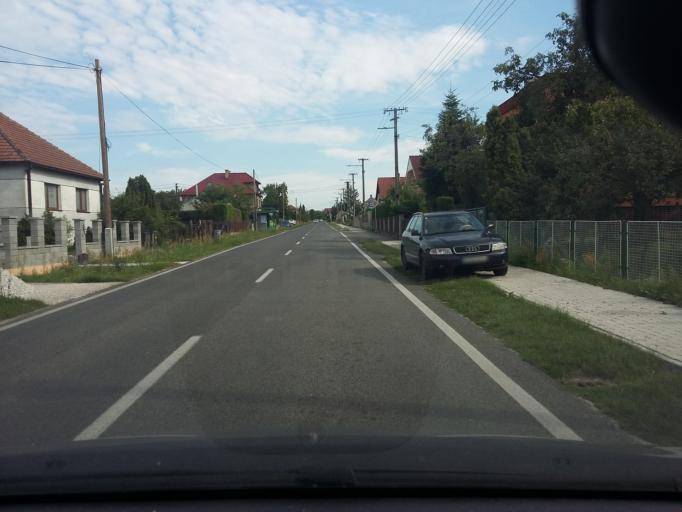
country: SK
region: Trnavsky
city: Gbely
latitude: 48.6362
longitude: 17.2015
